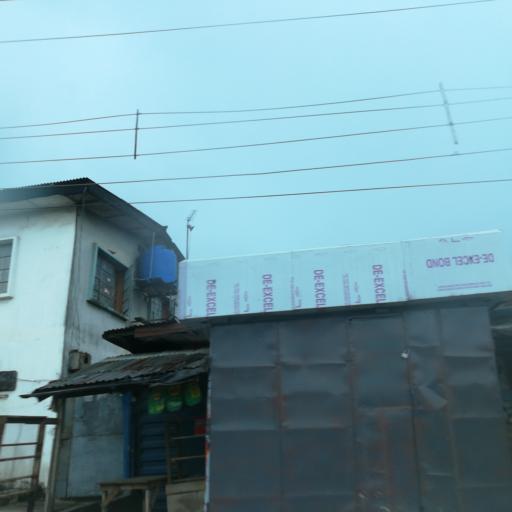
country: NG
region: Lagos
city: Oshodi
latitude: 6.5565
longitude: 3.3421
